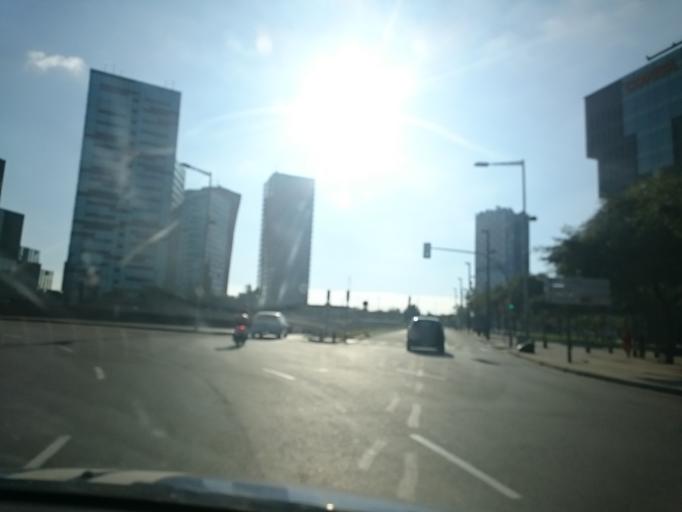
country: ES
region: Catalonia
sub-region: Provincia de Barcelona
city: L'Hospitalet de Llobregat
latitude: 41.3587
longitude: 2.1271
